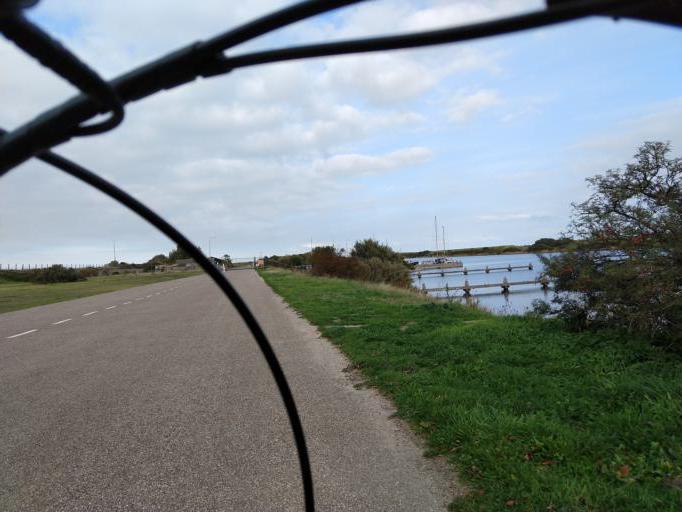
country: NL
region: South Holland
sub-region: Gemeente Goeree-Overflakkee
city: Goedereede
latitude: 51.7282
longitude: 3.9704
